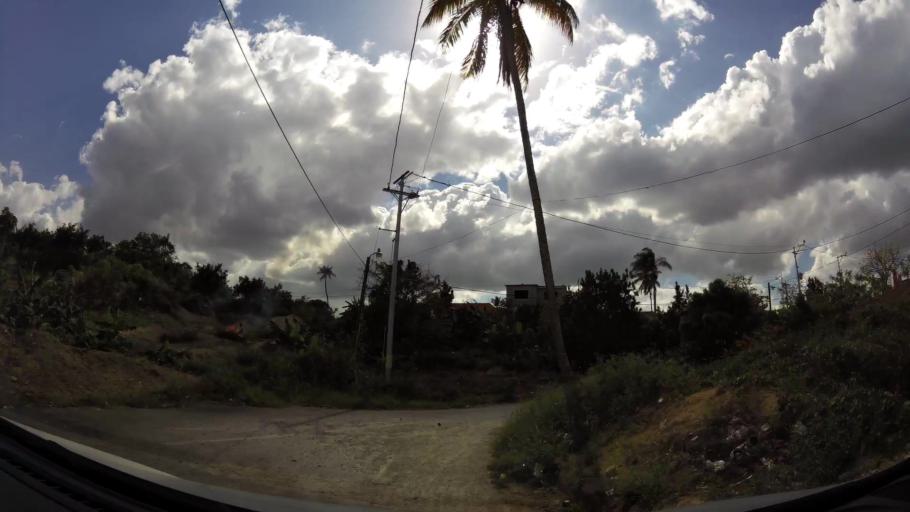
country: DO
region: Nacional
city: Ensanche Luperon
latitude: 18.5322
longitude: -69.8926
